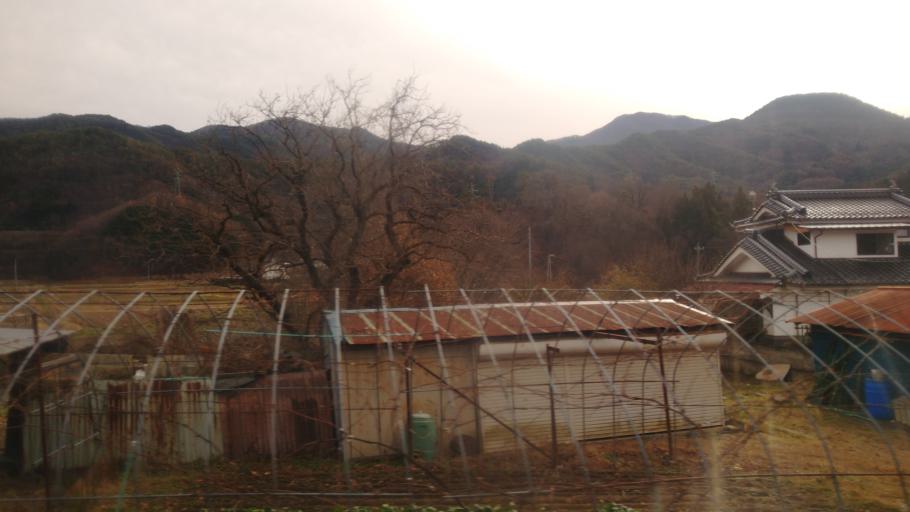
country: JP
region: Nagano
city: Omachi
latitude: 36.4466
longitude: 138.0353
